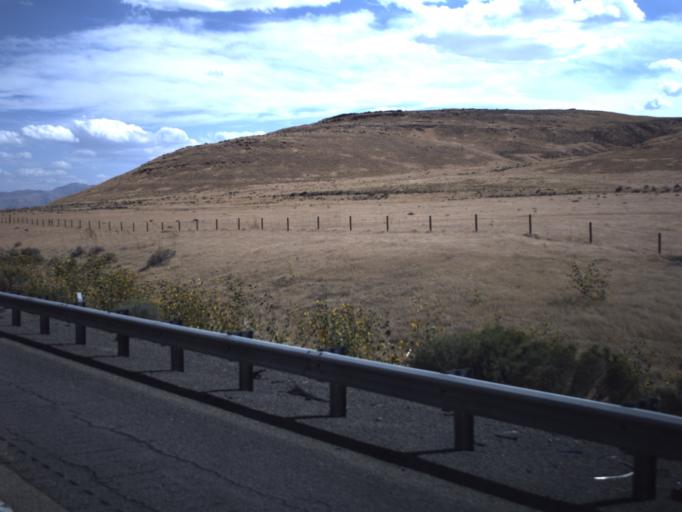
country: US
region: Utah
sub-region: Tooele County
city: Grantsville
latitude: 40.8221
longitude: -112.8914
